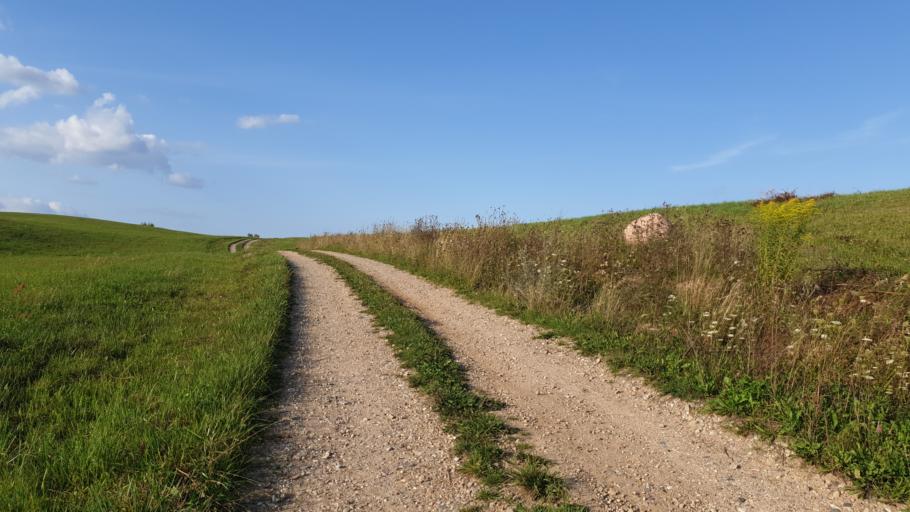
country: LT
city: Grigiskes
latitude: 54.7706
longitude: 25.0306
